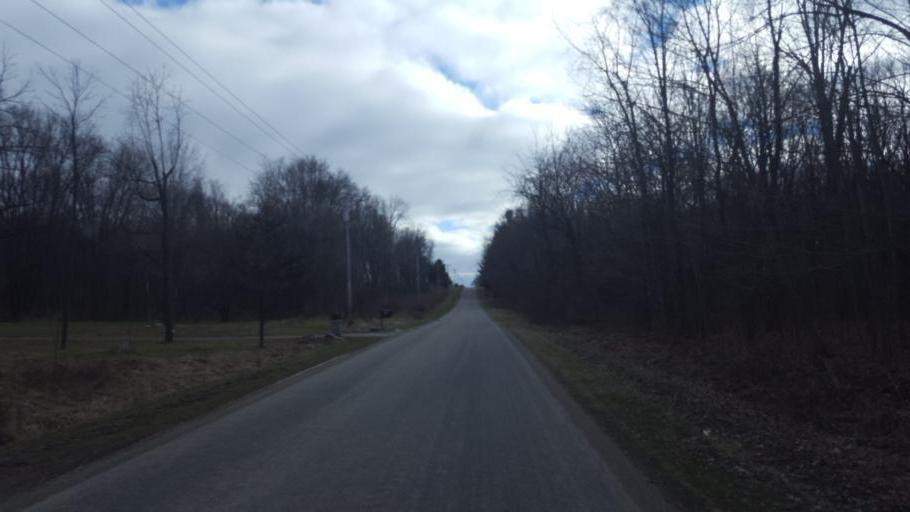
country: US
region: Ohio
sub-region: Morrow County
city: Mount Gilead
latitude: 40.5218
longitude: -82.7239
